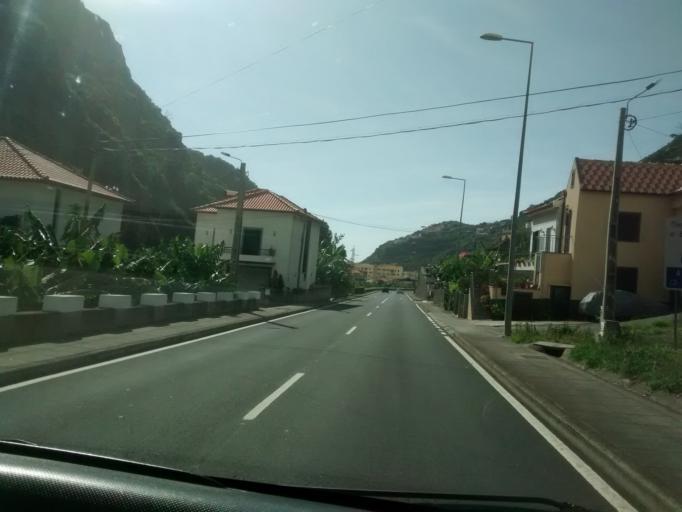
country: PT
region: Madeira
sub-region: Ribeira Brava
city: Campanario
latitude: 32.6826
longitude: -17.0544
